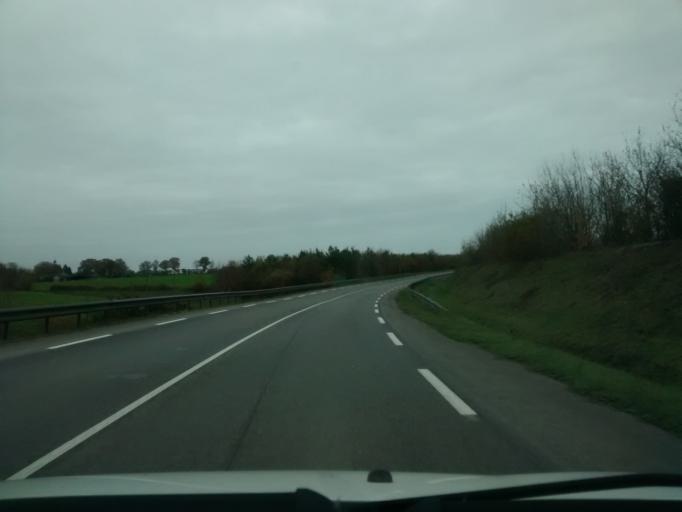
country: FR
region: Brittany
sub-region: Departement d'Ille-et-Vilaine
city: Etrelles
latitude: 48.0647
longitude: -1.1837
